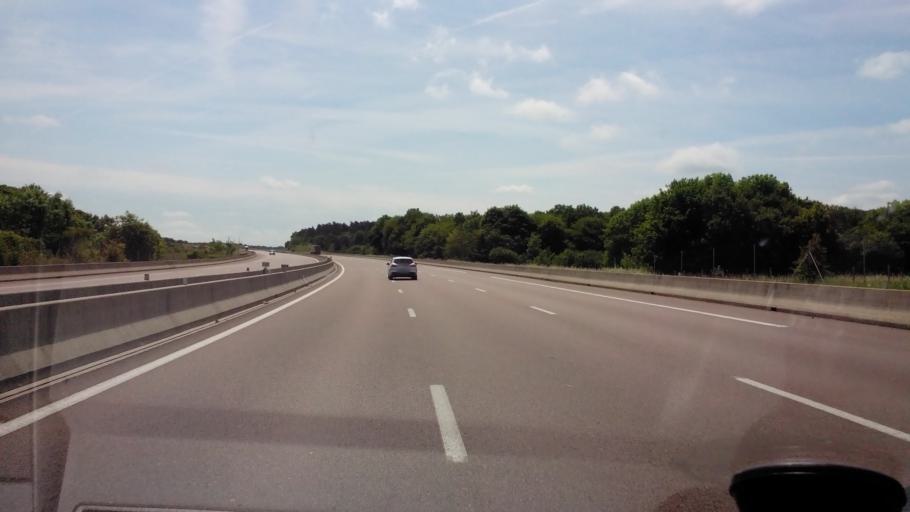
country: FR
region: Bourgogne
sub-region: Departement de la Cote-d'Or
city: Selongey
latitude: 47.7595
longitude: 5.1879
